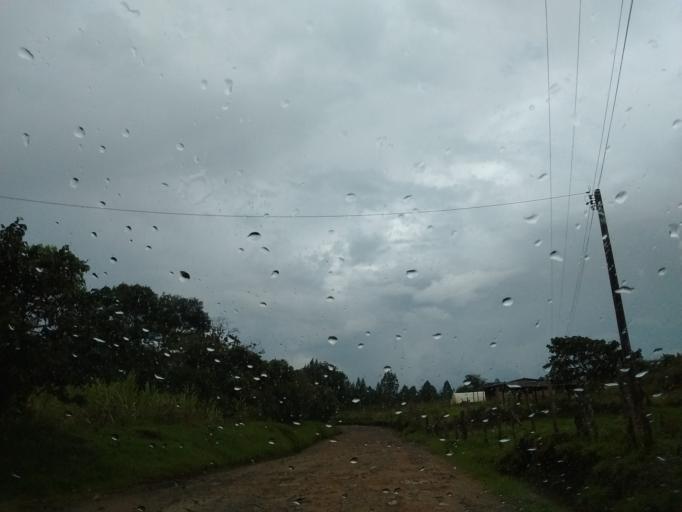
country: CO
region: Cauca
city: Cajibio
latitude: 2.5736
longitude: -76.6491
